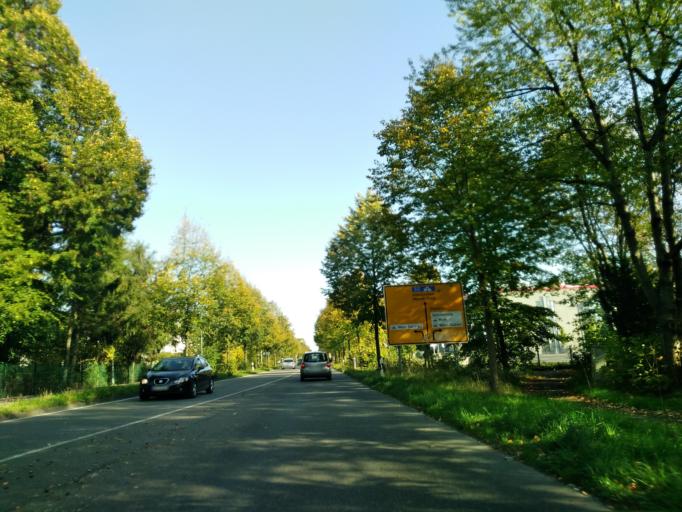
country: DE
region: North Rhine-Westphalia
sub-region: Regierungsbezirk Koln
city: Stossdorf
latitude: 50.7824
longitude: 7.2528
